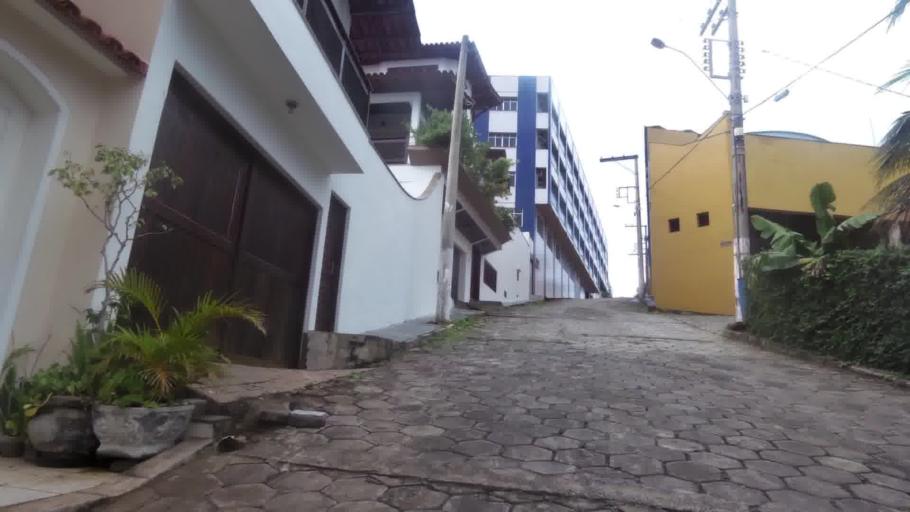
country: BR
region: Espirito Santo
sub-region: Piuma
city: Piuma
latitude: -20.8334
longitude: -40.6951
